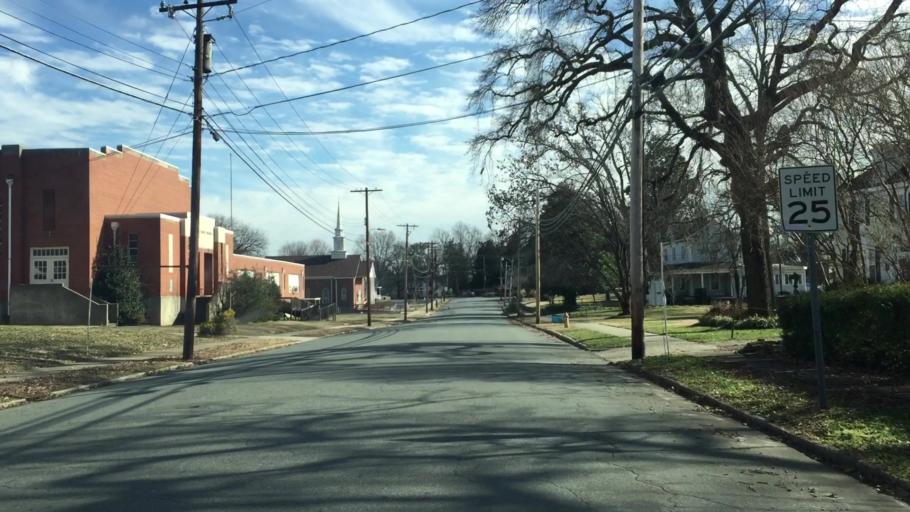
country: US
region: North Carolina
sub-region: Rockingham County
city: Reidsville
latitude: 36.3577
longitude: -79.6602
